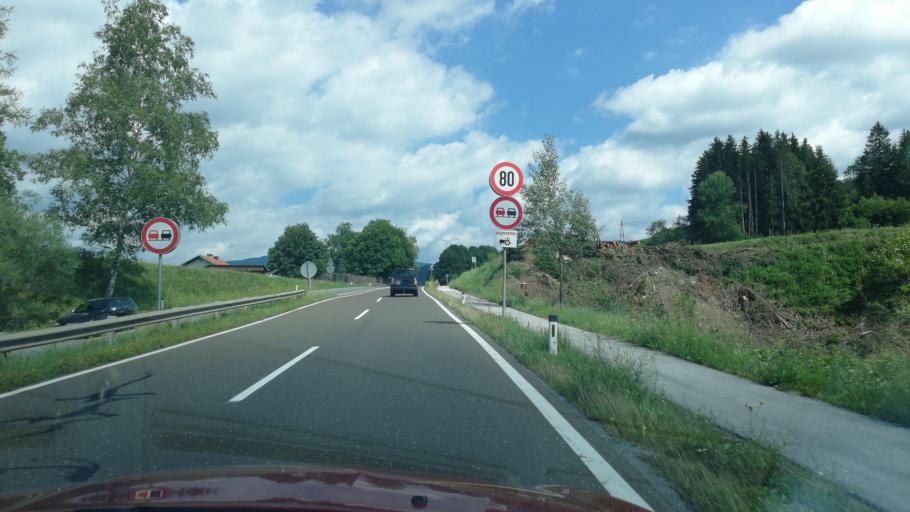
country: AT
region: Styria
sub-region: Politischer Bezirk Murau
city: Sankt Marein bei Neumarkt
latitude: 47.0522
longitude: 14.4332
